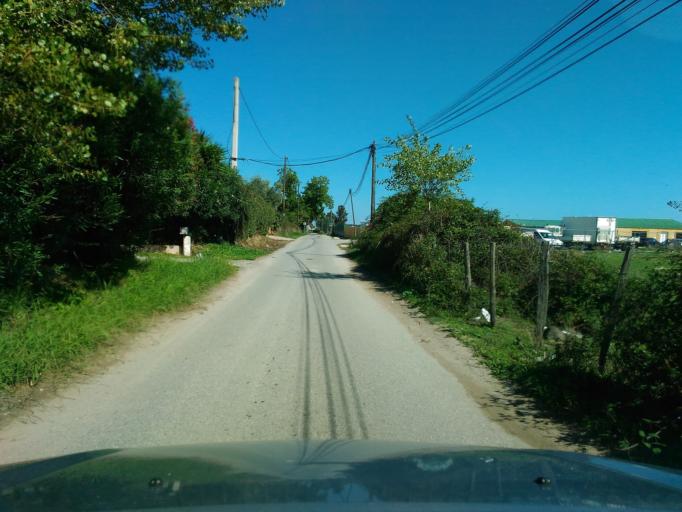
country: FR
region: Corsica
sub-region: Departement de la Haute-Corse
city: Aleria
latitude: 42.1074
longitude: 9.4767
